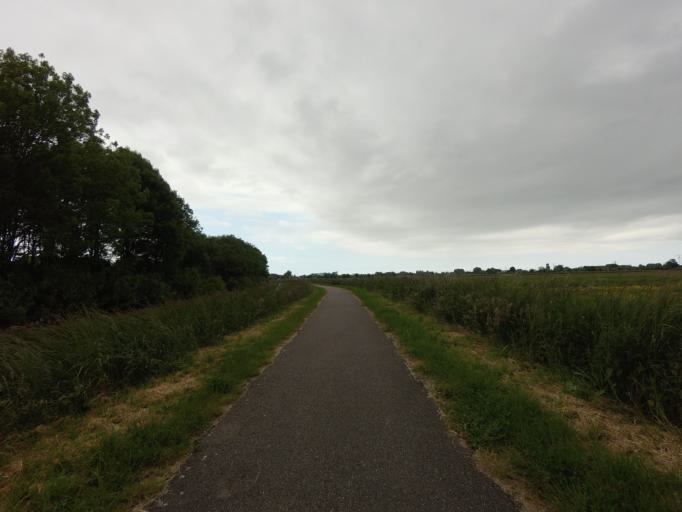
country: NL
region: North Holland
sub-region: Gemeente Hoorn
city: Hoorn
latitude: 52.6685
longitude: 5.0192
